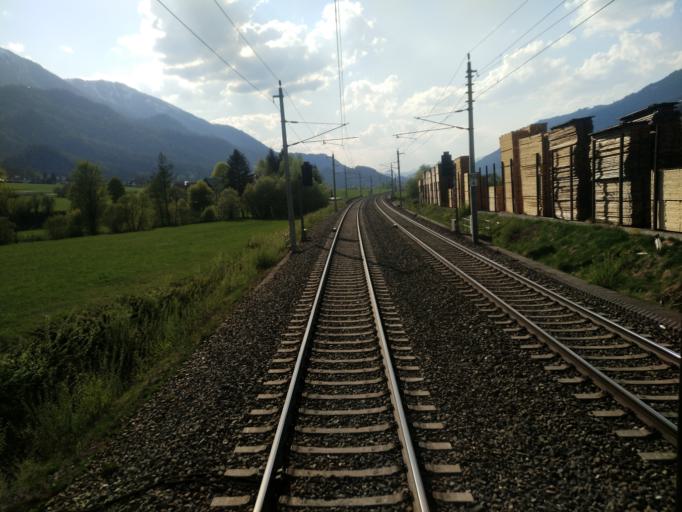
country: AT
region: Styria
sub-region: Politischer Bezirk Liezen
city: Trieben
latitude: 47.5135
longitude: 14.4267
